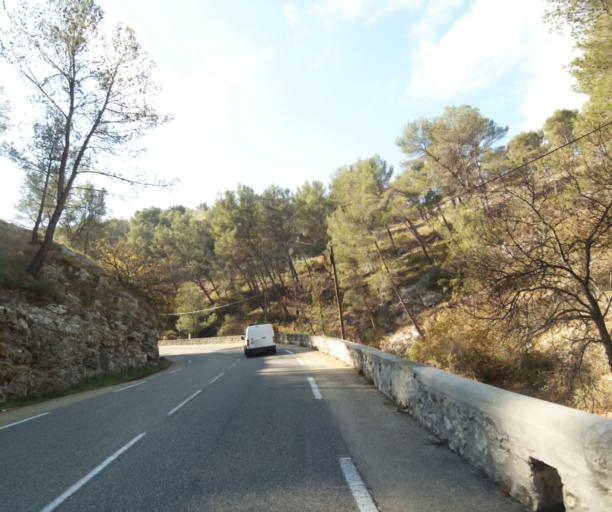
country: FR
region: Provence-Alpes-Cote d'Azur
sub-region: Departement des Bouches-du-Rhone
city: Saint-Savournin
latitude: 43.3700
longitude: 5.5114
